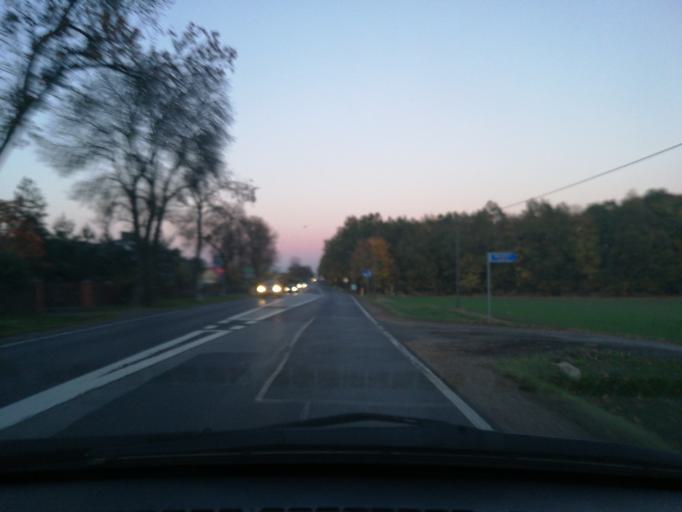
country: PL
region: Lodz Voivodeship
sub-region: Powiat lodzki wschodni
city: Andrespol
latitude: 51.7974
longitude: 19.6333
